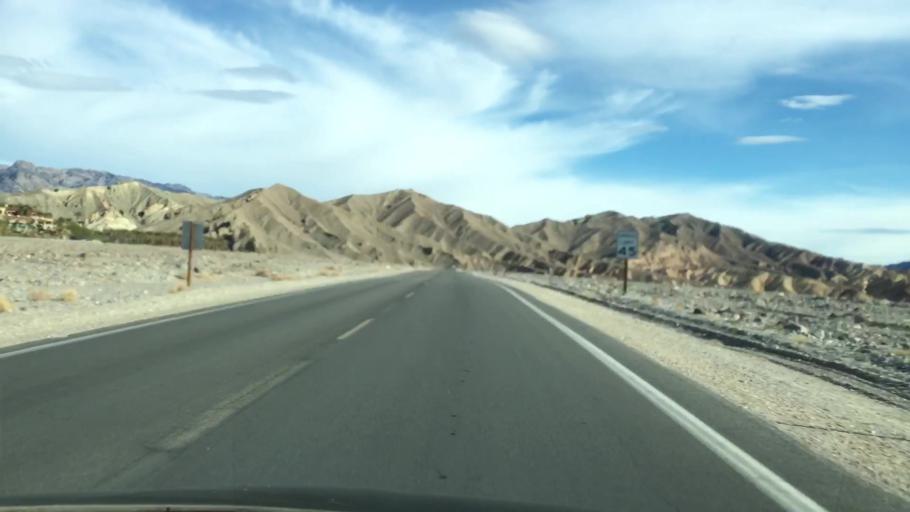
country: US
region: Nevada
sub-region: Nye County
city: Beatty
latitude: 36.4501
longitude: -116.8592
